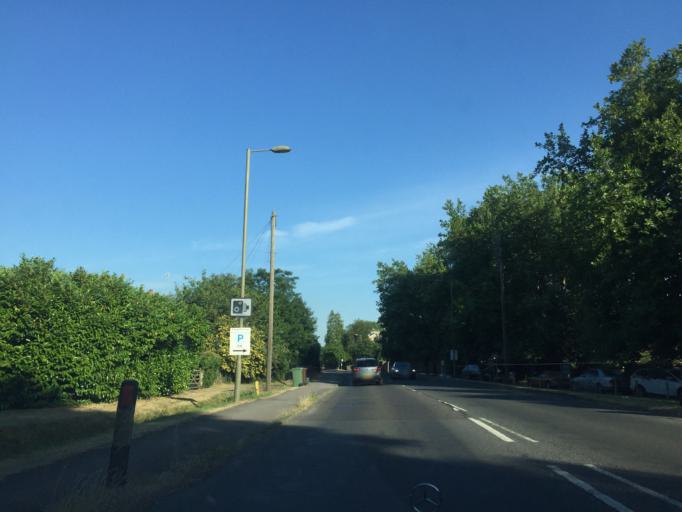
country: GB
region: England
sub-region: Oxfordshire
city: Henley on Thames
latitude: 51.5455
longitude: -0.9129
